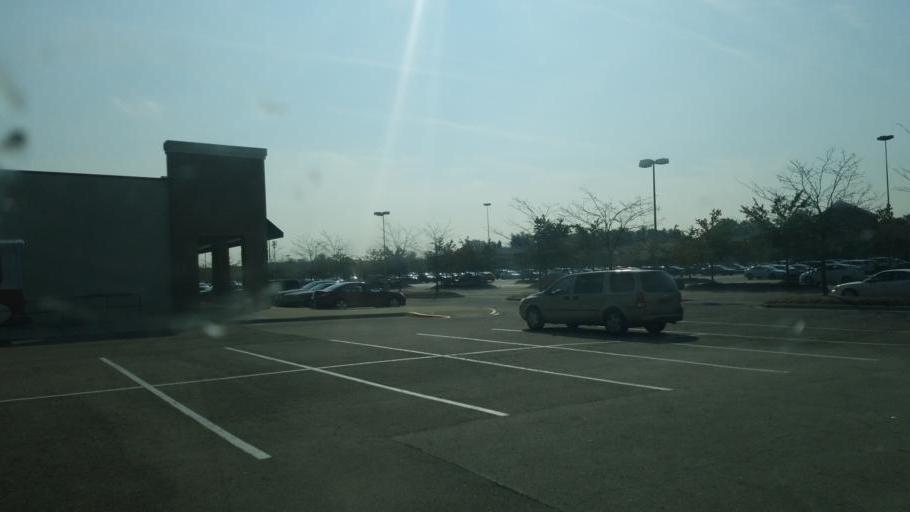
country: US
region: Ohio
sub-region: Franklin County
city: Worthington
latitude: 40.0665
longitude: -83.0260
